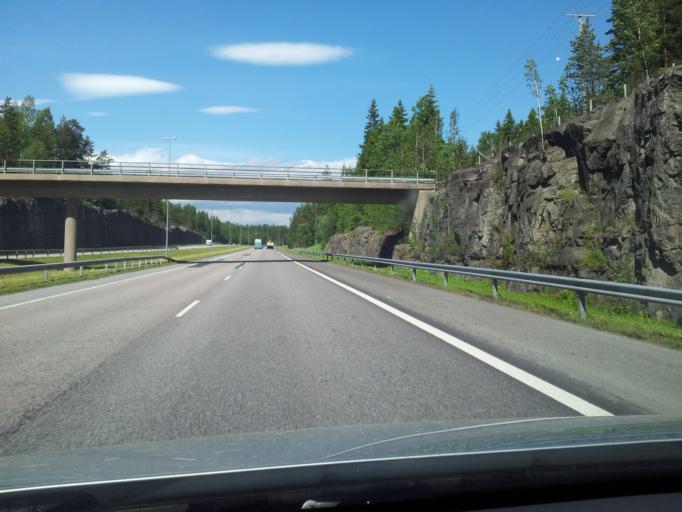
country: FI
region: Uusimaa
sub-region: Porvoo
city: Porvoo
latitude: 60.3467
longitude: 25.5145
